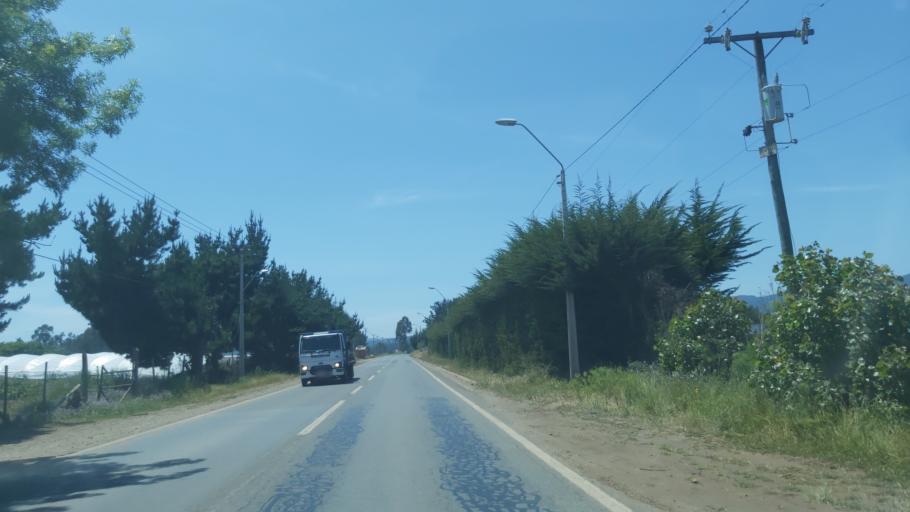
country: CL
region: Maule
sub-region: Provincia de Cauquenes
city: Cauquenes
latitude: -35.7972
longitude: -72.5566
